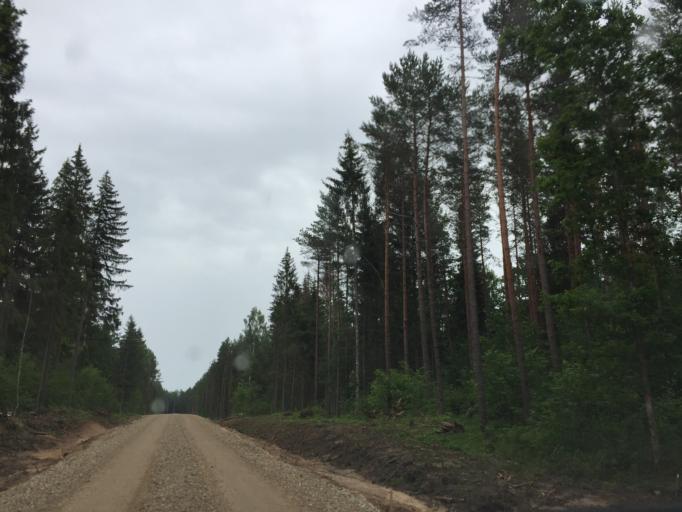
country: LV
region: Tukuma Rajons
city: Tukums
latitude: 57.0057
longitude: 23.1022
